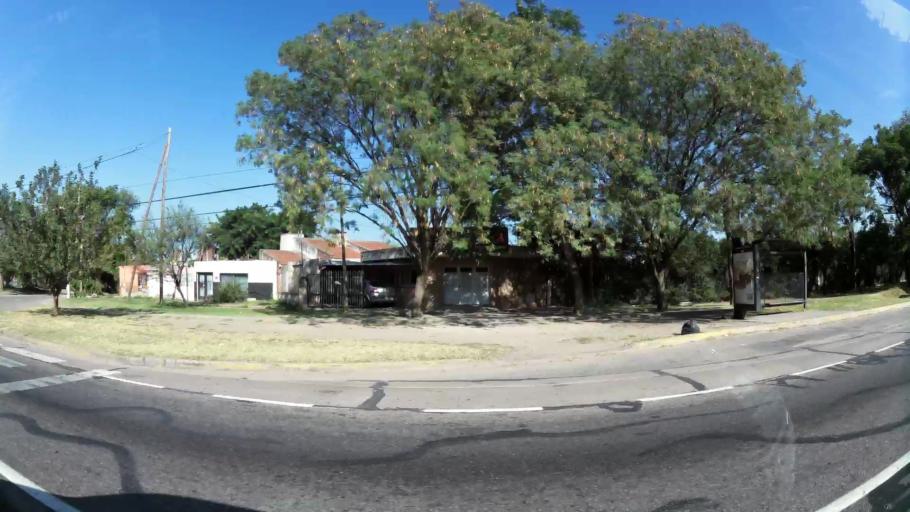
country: AR
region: Cordoba
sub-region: Departamento de Capital
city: Cordoba
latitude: -31.4822
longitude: -64.2424
